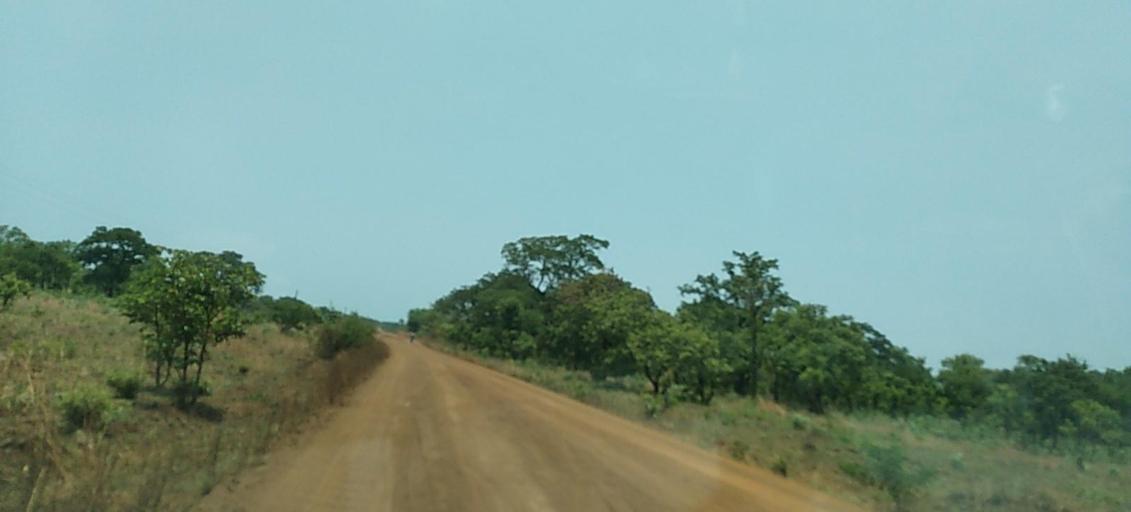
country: ZM
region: Copperbelt
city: Mpongwe
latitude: -13.6982
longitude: 27.8659
